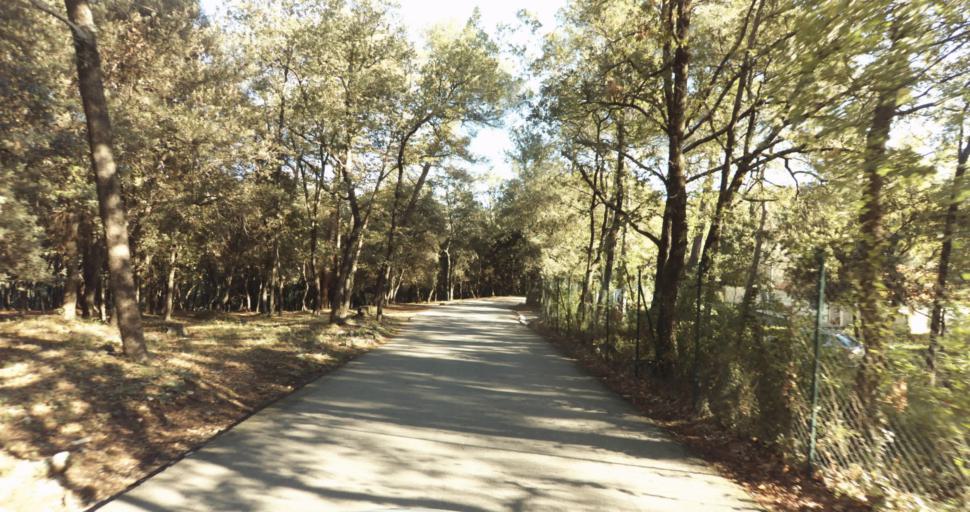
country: FR
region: Provence-Alpes-Cote d'Azur
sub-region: Departement des Alpes-Maritimes
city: Vence
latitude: 43.7131
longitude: 7.0984
